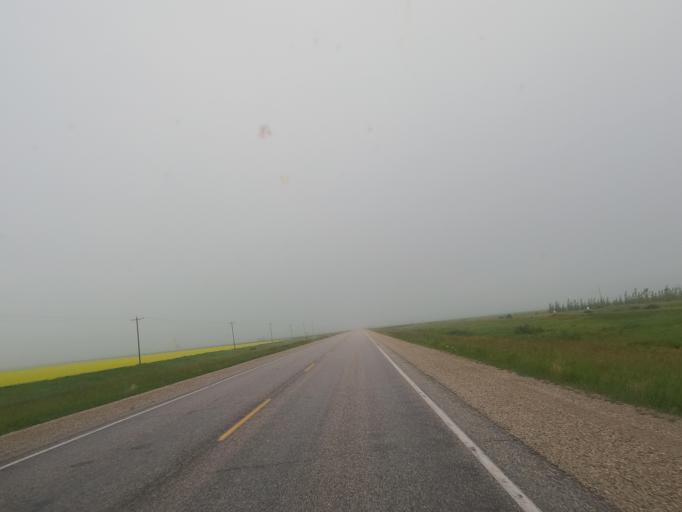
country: CA
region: Manitoba
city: Carman
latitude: 49.6936
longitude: -97.9567
